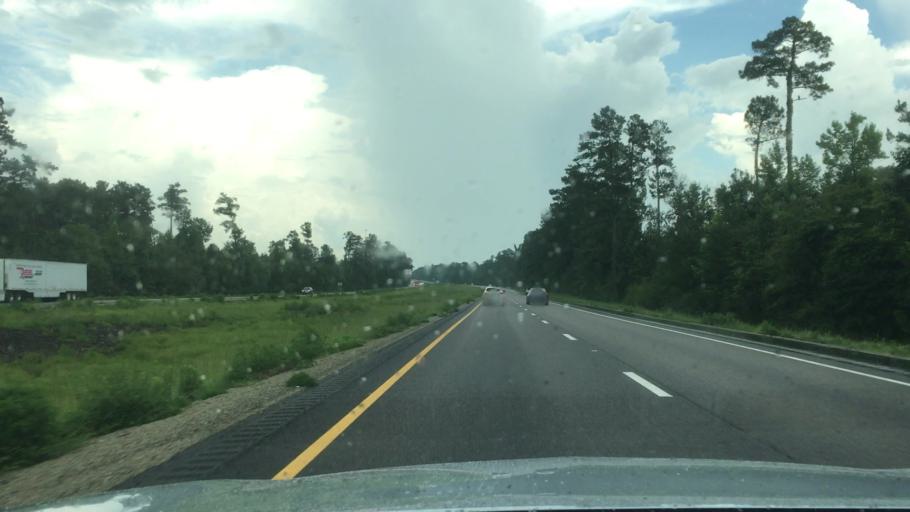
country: US
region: Mississippi
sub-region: Lamar County
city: Purvis
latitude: 31.1730
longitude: -89.3498
